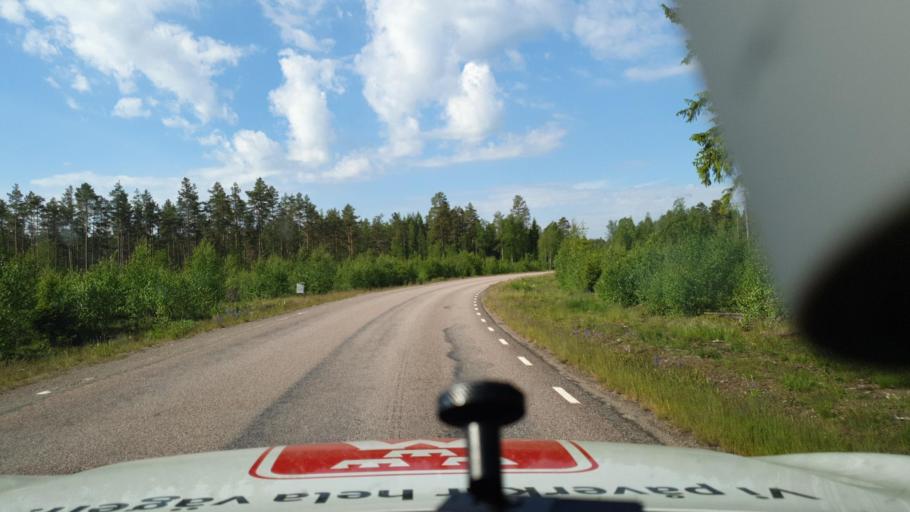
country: SE
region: Vaermland
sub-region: Arvika Kommun
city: Arvika
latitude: 59.9382
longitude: 12.6748
